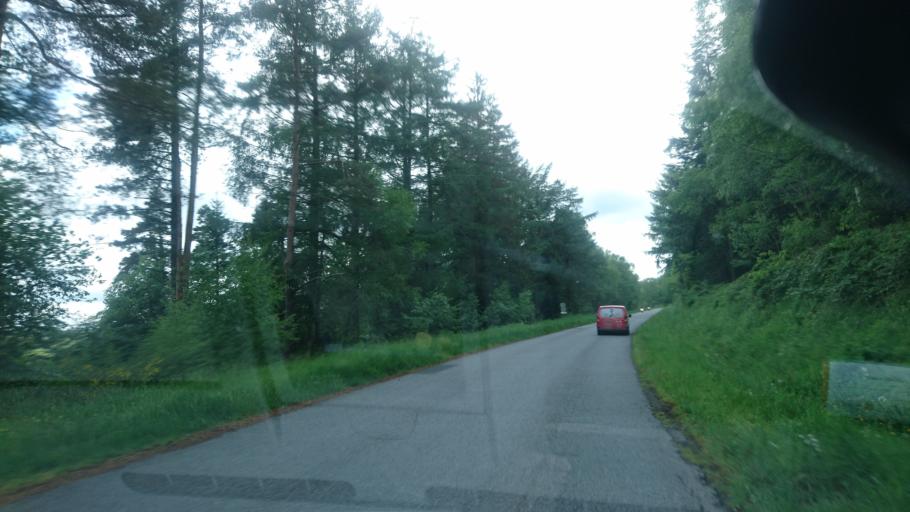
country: FR
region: Limousin
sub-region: Departement de la Haute-Vienne
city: Peyrat-le-Chateau
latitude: 45.8065
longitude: 1.9065
